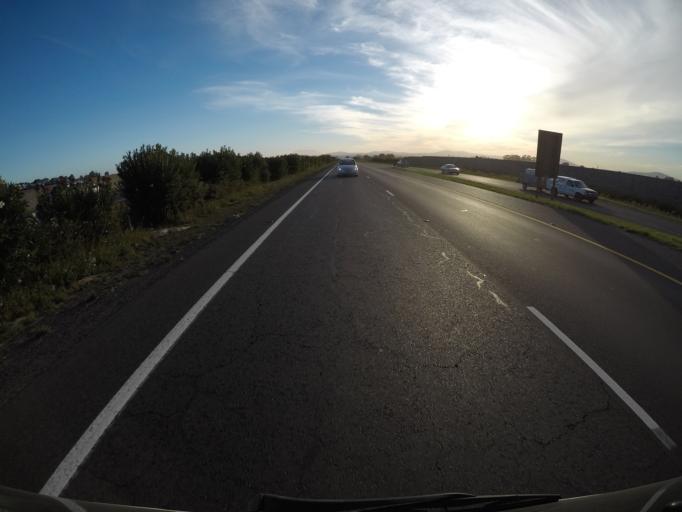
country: ZA
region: Western Cape
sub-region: City of Cape Town
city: Kraaifontein
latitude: -33.8282
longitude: 18.7612
